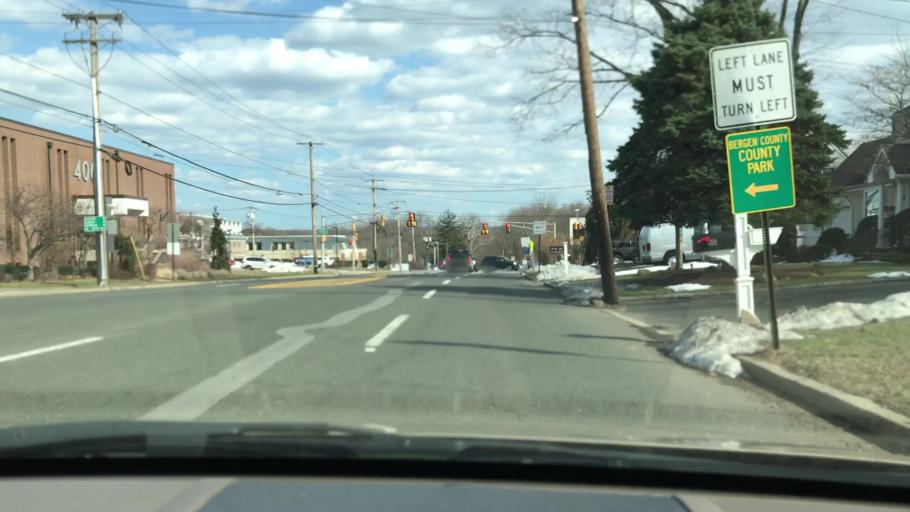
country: US
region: New Jersey
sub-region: Bergen County
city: River Vale
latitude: 40.9823
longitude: -74.0082
